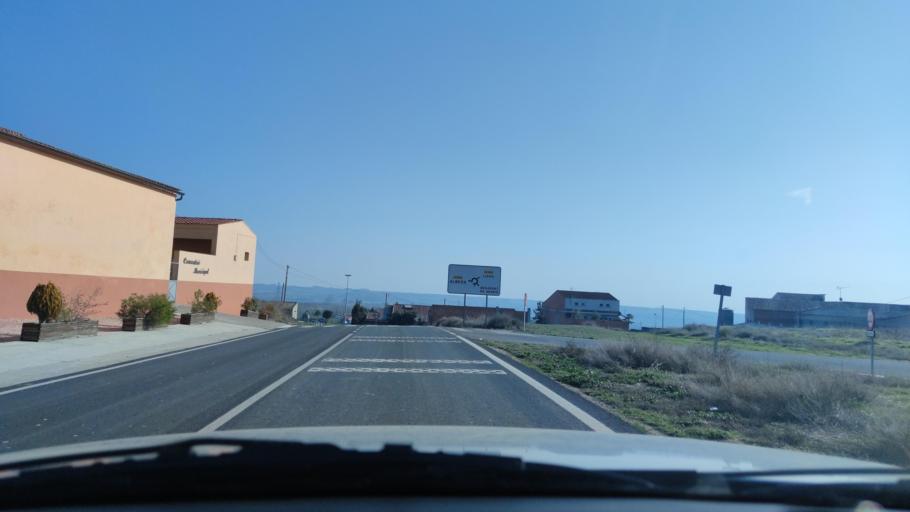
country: ES
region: Catalonia
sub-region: Provincia de Lleida
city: Torrefarrera
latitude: 41.6991
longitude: 0.6320
